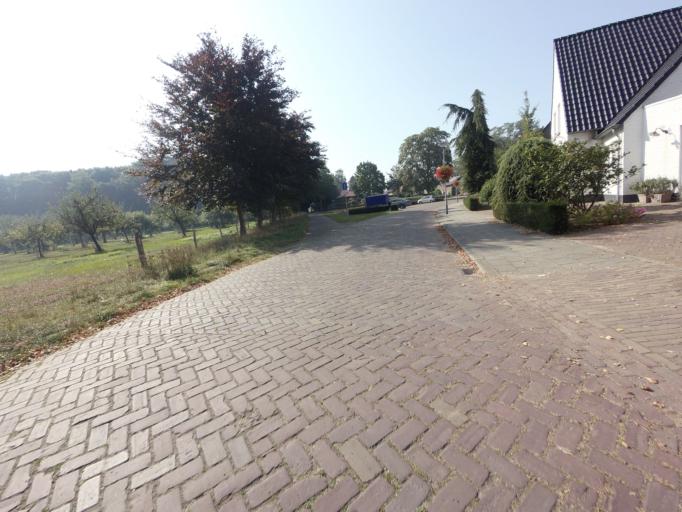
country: NL
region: Limburg
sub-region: Gemeente Beesel
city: Beesel
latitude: 51.2669
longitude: 6.0411
